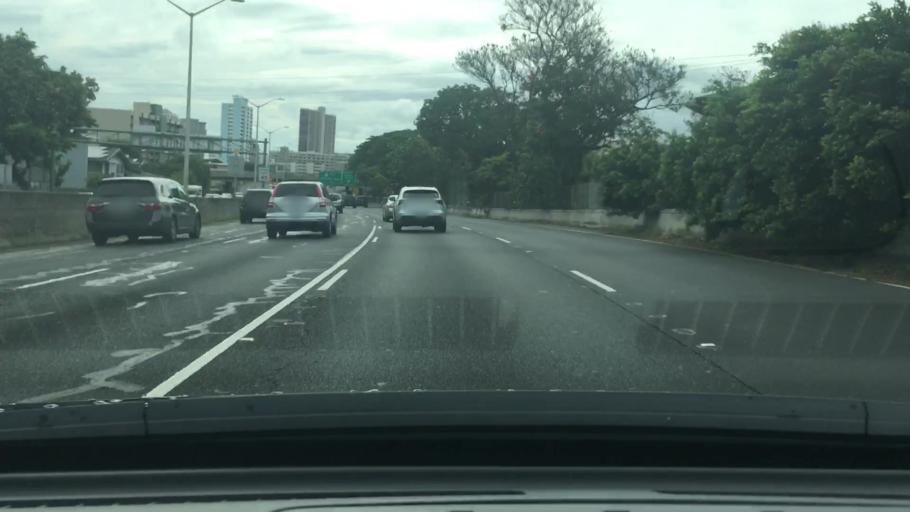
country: US
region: Hawaii
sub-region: Honolulu County
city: Honolulu
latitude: 21.3021
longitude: -157.8360
